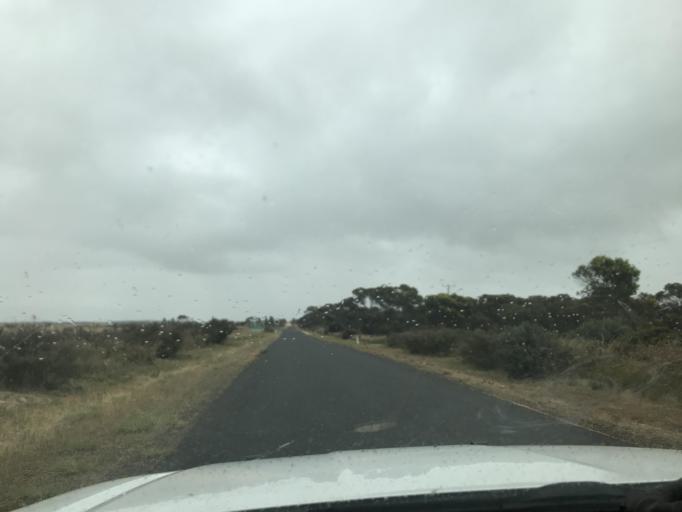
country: AU
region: South Australia
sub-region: Tatiara
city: Bordertown
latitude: -36.1161
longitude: 141.0293
